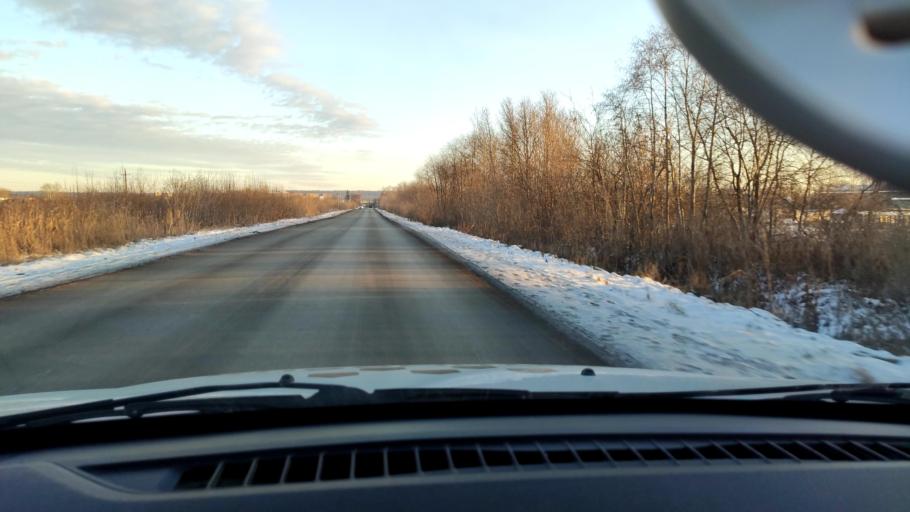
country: RU
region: Perm
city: Ferma
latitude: 57.9016
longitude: 56.2880
